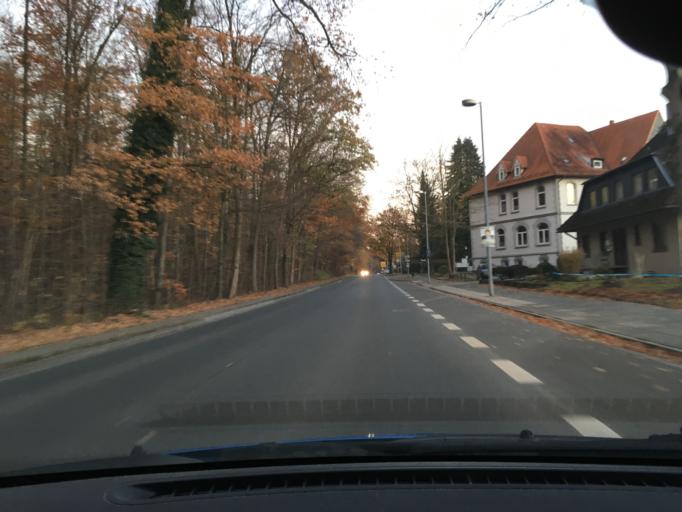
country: DE
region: Lower Saxony
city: Uelzen
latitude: 52.9754
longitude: 10.5479
